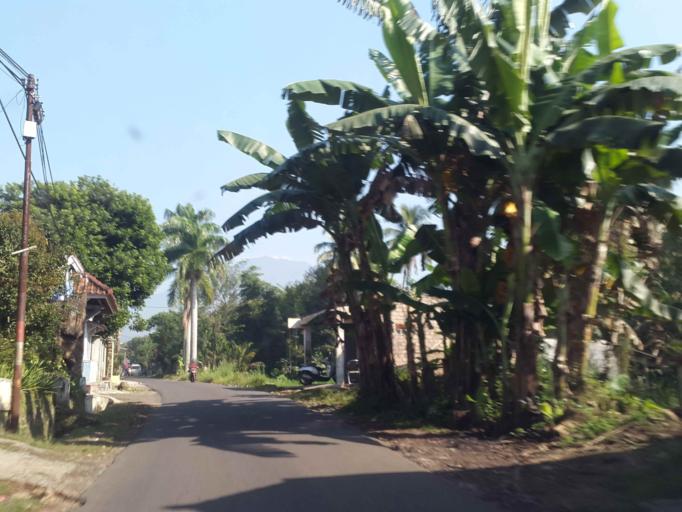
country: ID
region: West Java
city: Cibeber
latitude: -6.8674
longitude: 107.0888
